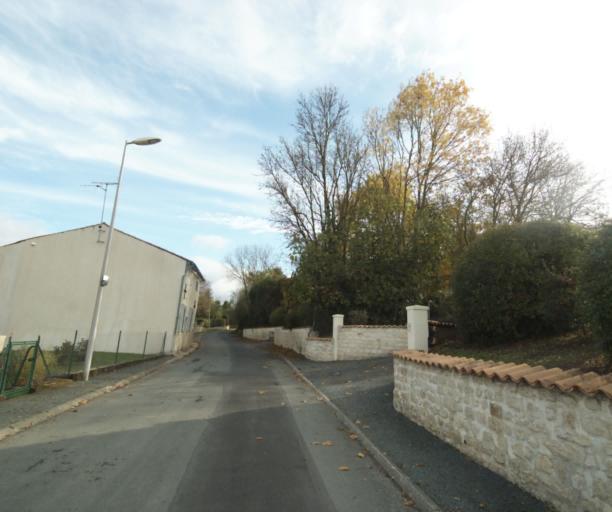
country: FR
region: Poitou-Charentes
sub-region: Departement de la Charente-Maritime
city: Saint-Georges-des-Coteaux
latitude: 45.7621
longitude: -0.7124
